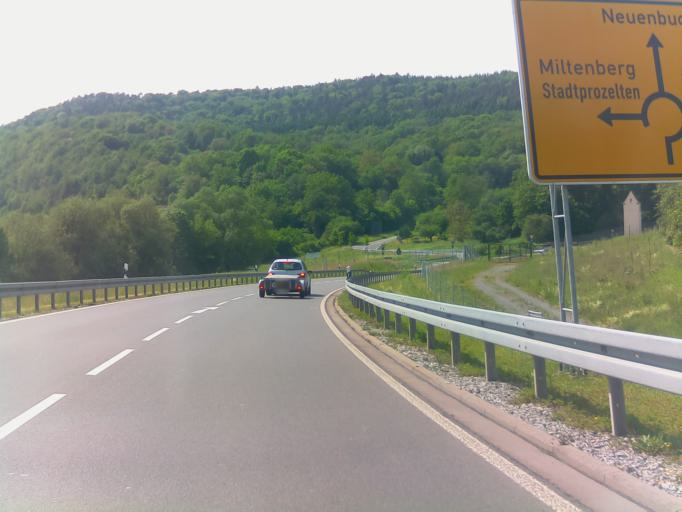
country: DE
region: Bavaria
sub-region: Regierungsbezirk Unterfranken
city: Faulbach
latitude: 49.7921
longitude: 9.4366
